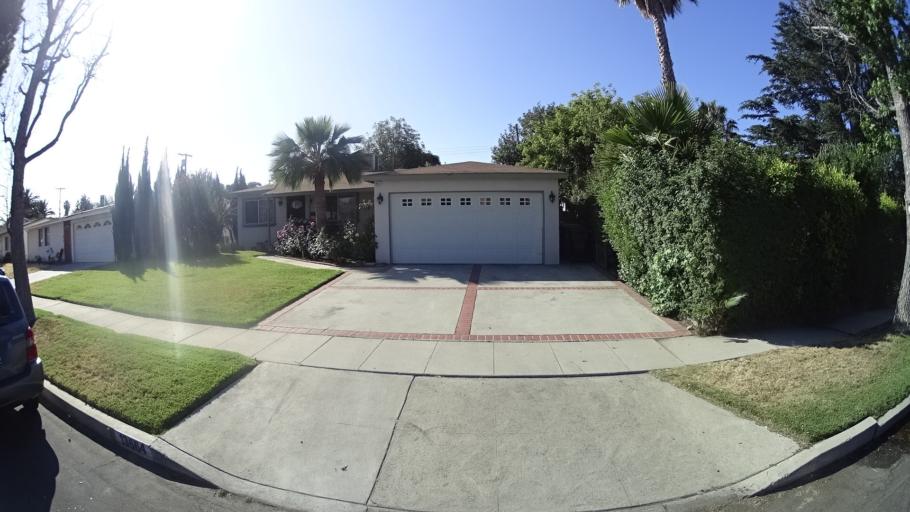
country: US
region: California
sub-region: Los Angeles County
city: Van Nuys
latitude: 34.2263
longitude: -118.4300
